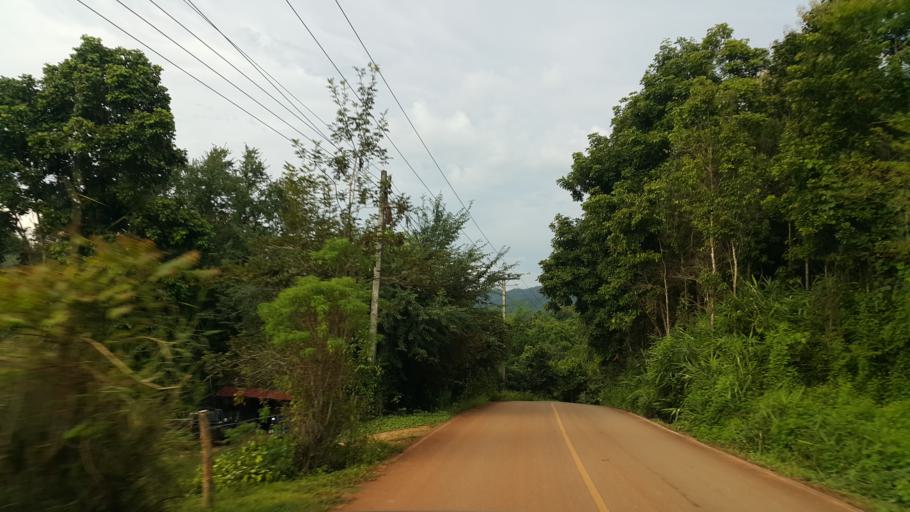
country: TH
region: Chiang Mai
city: Mae On
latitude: 18.8986
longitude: 99.2360
